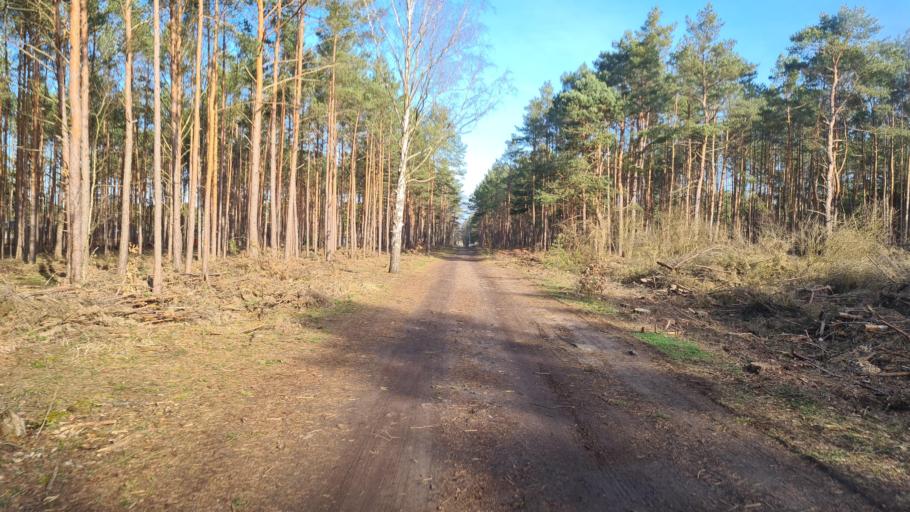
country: DE
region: Brandenburg
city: Gross Koris
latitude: 52.1577
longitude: 13.6930
